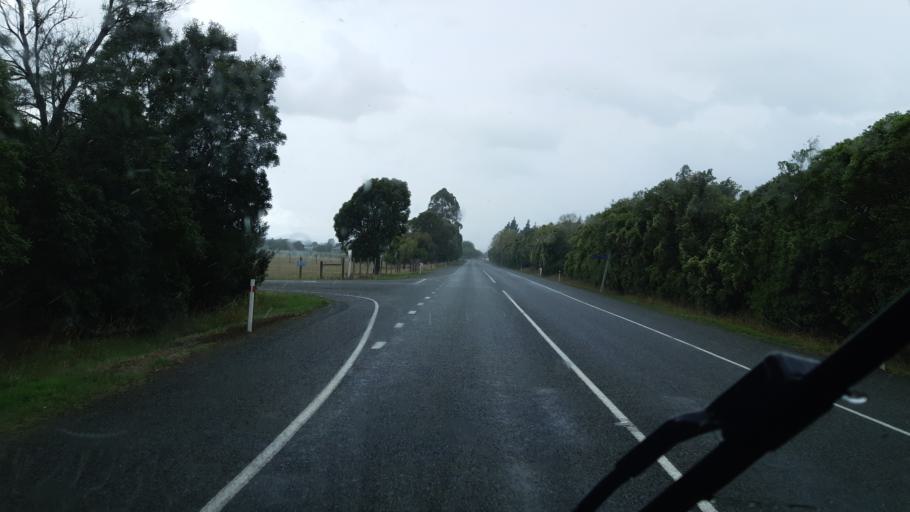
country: NZ
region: Tasman
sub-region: Tasman District
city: Brightwater
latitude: -41.3801
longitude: 173.0906
